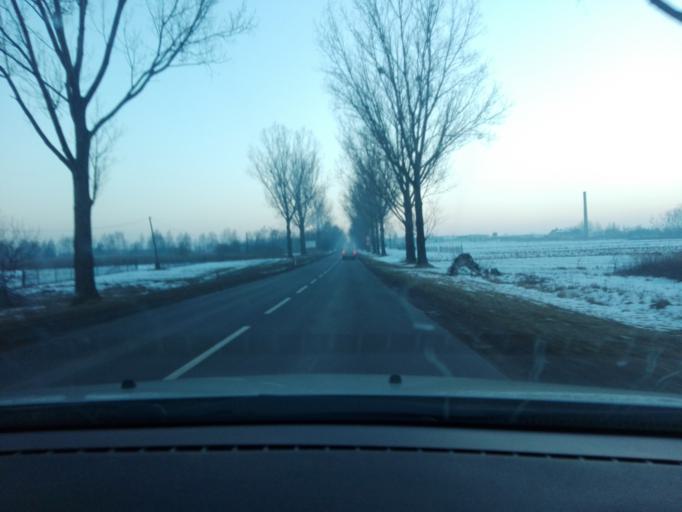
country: PL
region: Lodz Voivodeship
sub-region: Powiat zgierski
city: Zgierz
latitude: 51.9004
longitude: 19.4259
